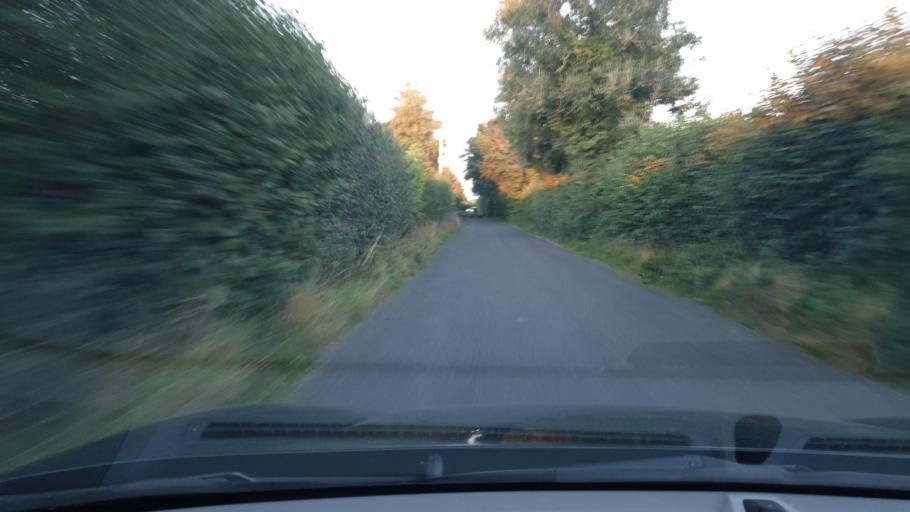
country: IE
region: Leinster
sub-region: Kildare
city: Prosperous
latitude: 53.3253
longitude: -6.7918
